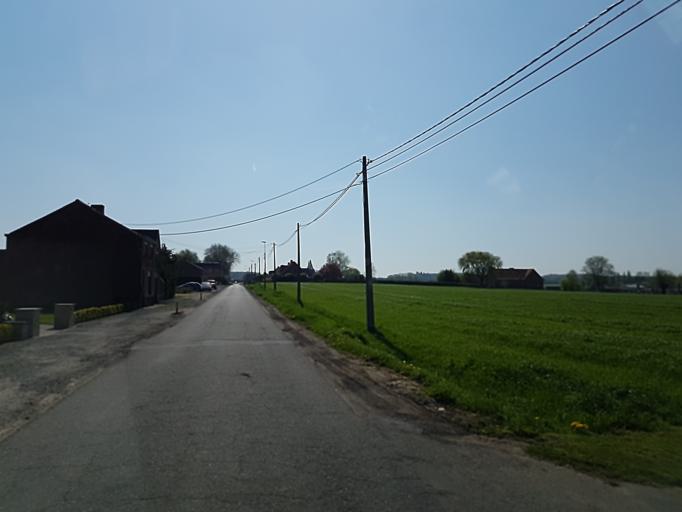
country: BE
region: Flanders
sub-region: Provincie West-Vlaanderen
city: Zonnebeke
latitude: 50.8608
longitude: 2.9562
